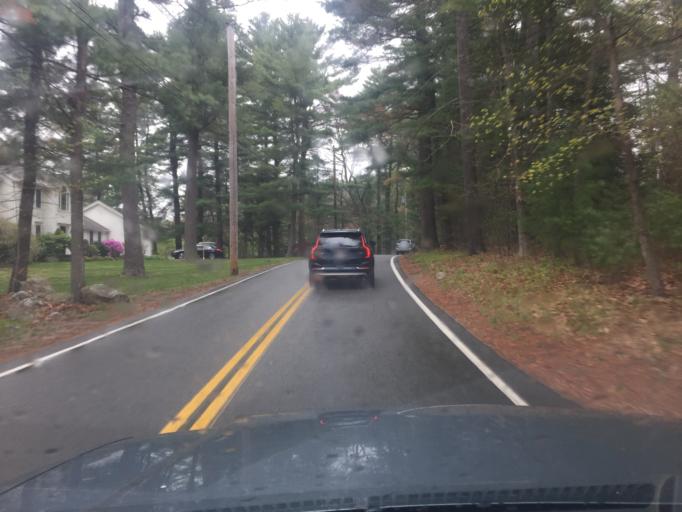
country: US
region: Massachusetts
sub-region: Norfolk County
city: Dover
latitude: 42.2233
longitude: -71.2637
